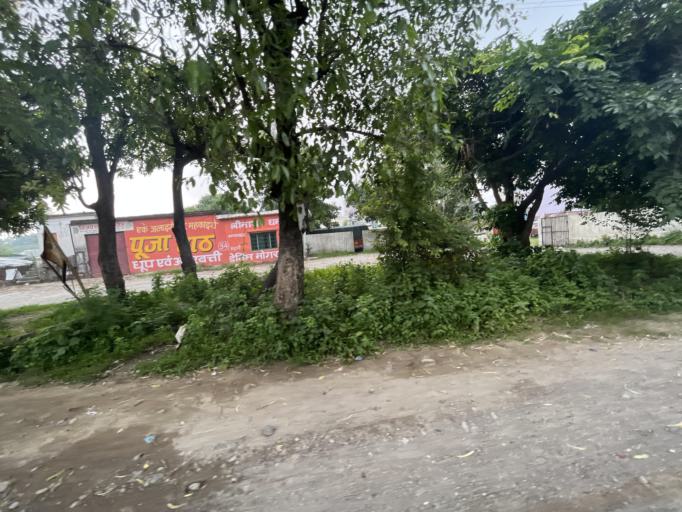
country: IN
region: Uttarakhand
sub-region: Naini Tal
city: Haldwani
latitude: 29.1983
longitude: 79.5131
